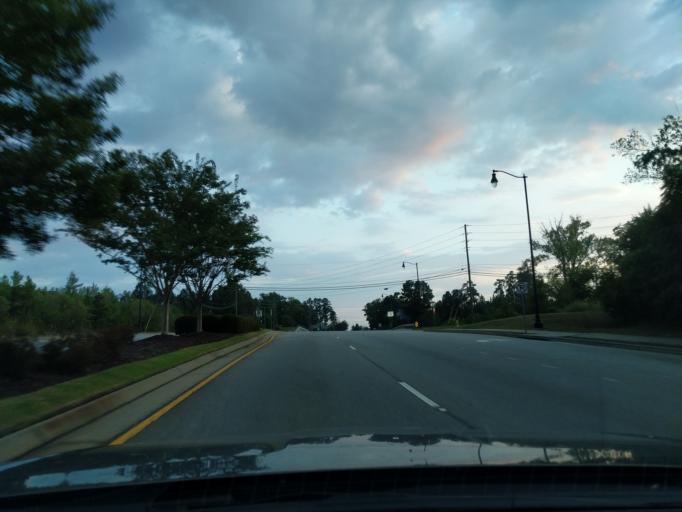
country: US
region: Georgia
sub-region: Columbia County
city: Martinez
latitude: 33.5179
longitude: -82.0245
